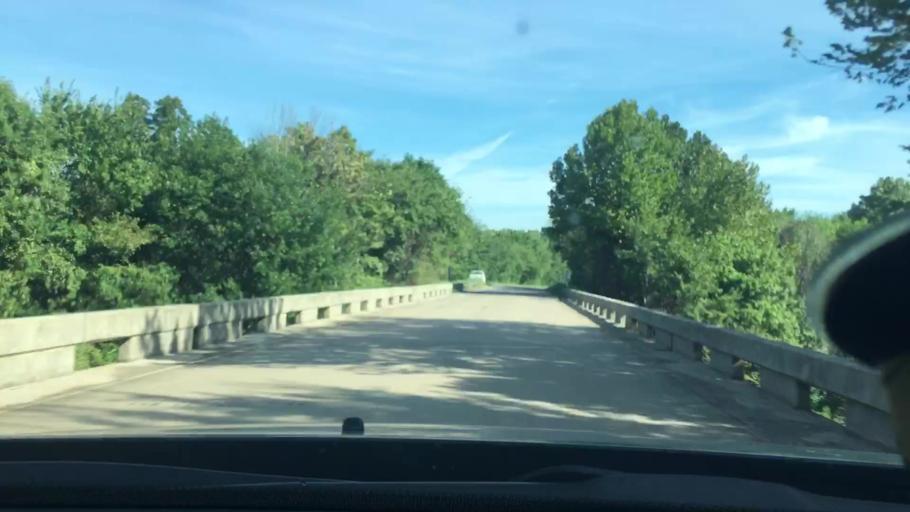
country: US
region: Oklahoma
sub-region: Carter County
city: Lone Grove
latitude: 34.2840
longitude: -97.2827
